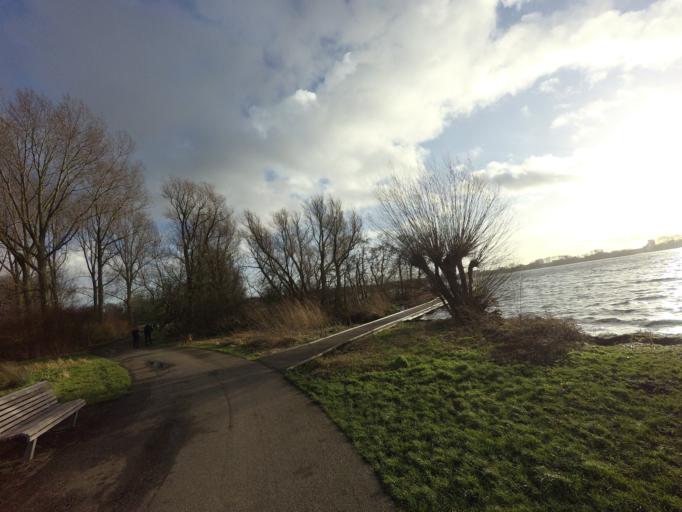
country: NL
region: South Holland
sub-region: Gemeente Rotterdam
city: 's-Gravenland
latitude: 51.9406
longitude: 4.5172
